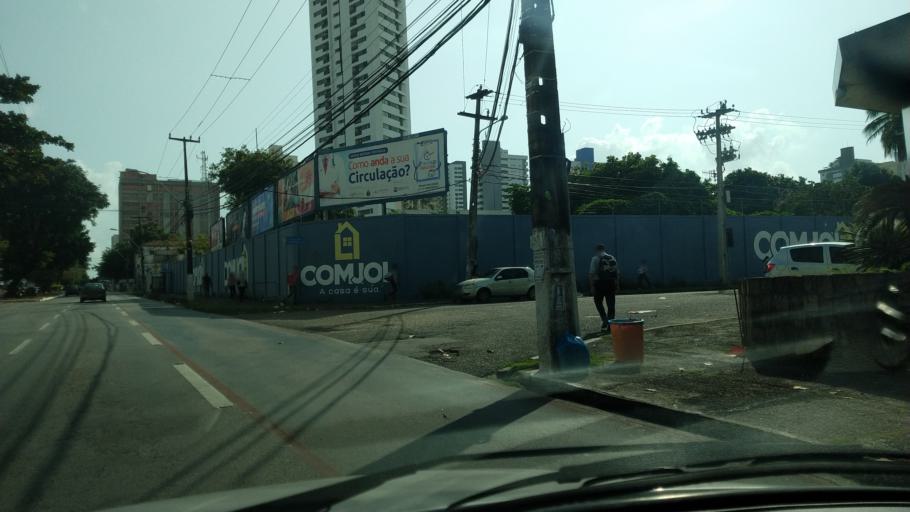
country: BR
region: Rio Grande do Norte
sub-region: Natal
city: Natal
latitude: -5.7926
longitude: -35.2030
